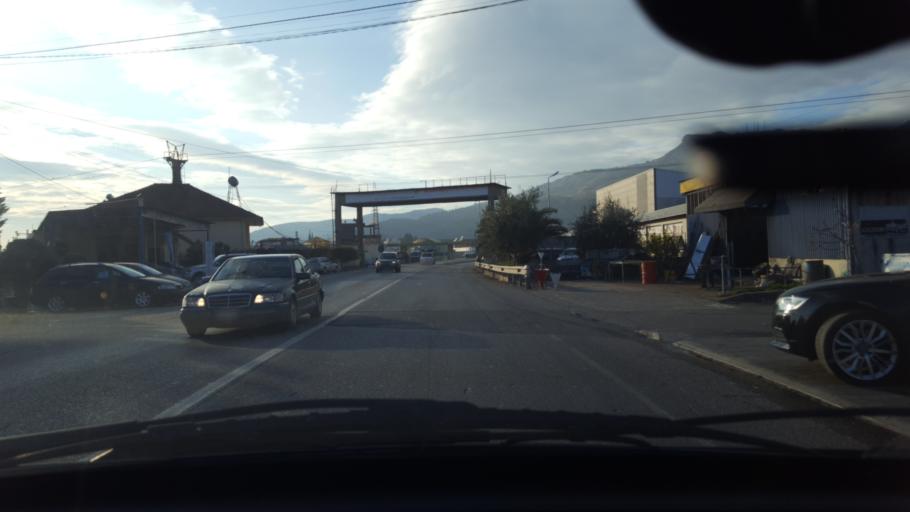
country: AL
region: Elbasan
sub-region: Rrethi i Elbasanit
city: Bradashesh
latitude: 41.0990
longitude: 20.0374
